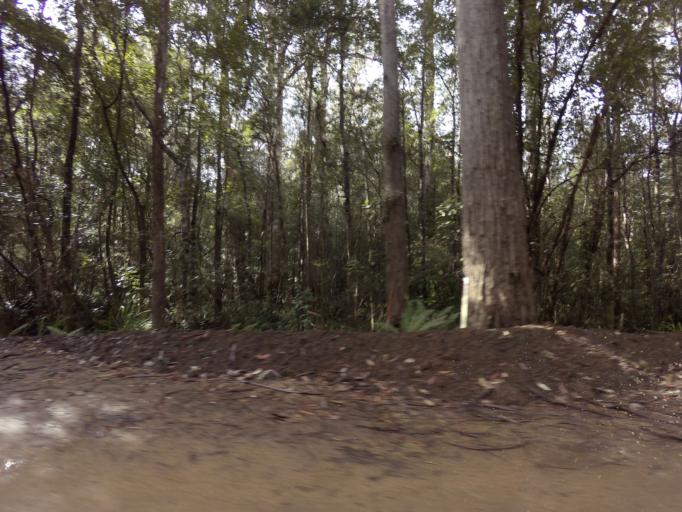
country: AU
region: Tasmania
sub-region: Huon Valley
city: Geeveston
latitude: -43.5732
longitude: 146.8886
